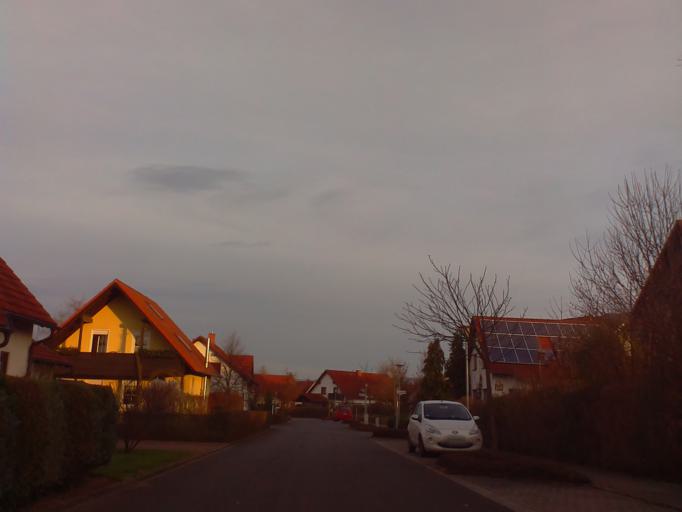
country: DE
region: Thuringia
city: Rothenstein
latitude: 50.8429
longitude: 11.6075
